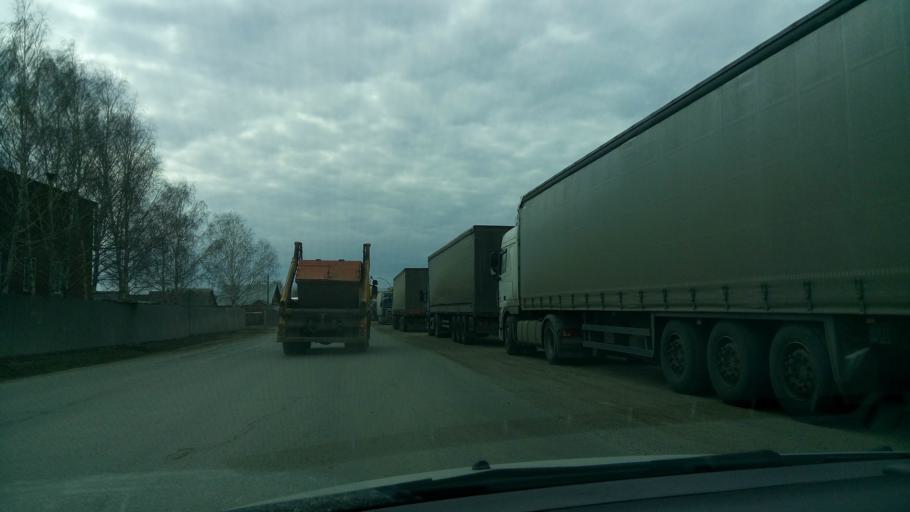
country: RU
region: Sverdlovsk
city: Verkhnyaya Pyshma
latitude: 56.9577
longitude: 60.6689
